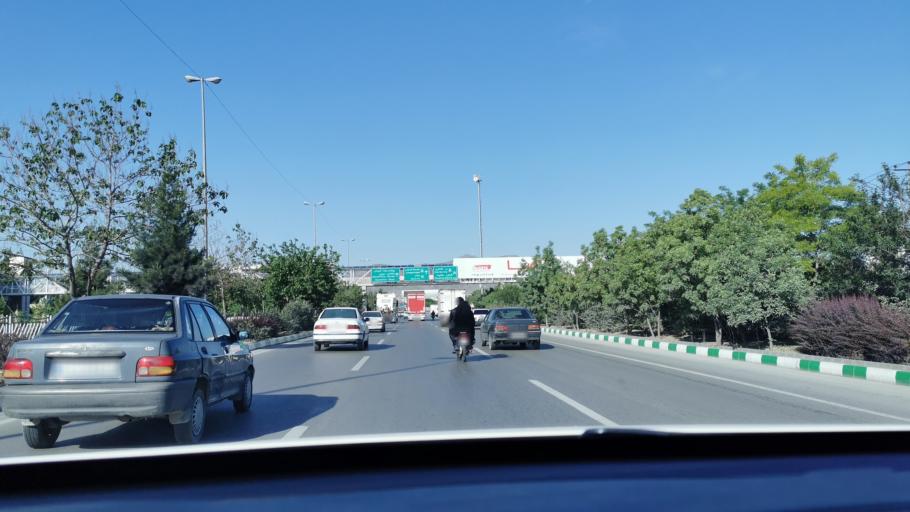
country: IR
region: Razavi Khorasan
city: Mashhad
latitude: 36.2564
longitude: 59.6209
